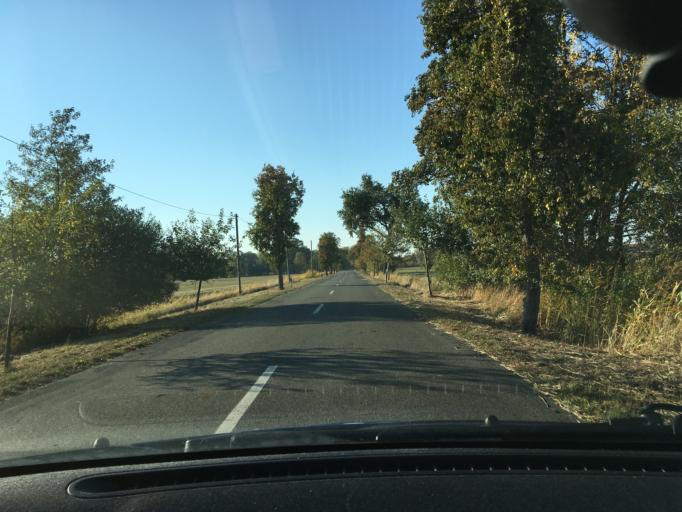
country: DE
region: Lower Saxony
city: Hitzacker
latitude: 53.1538
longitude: 11.0824
